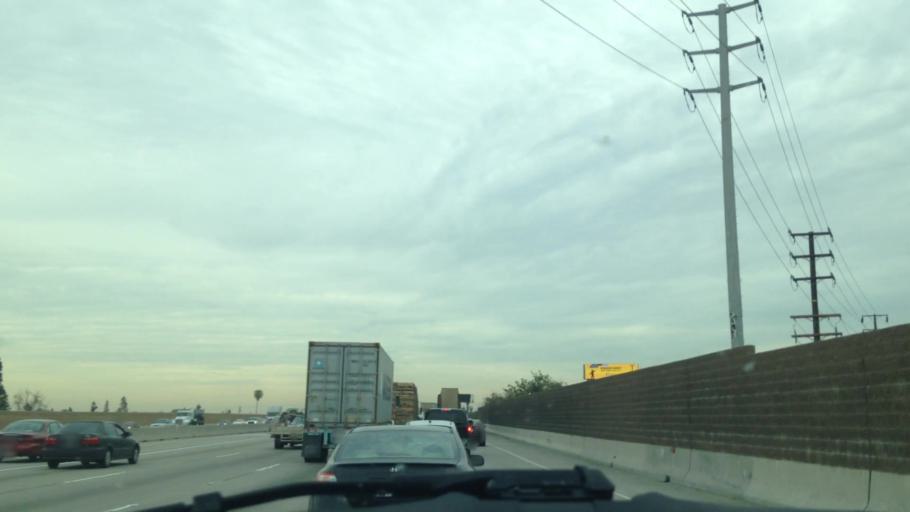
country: US
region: California
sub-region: Orange County
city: Placentia
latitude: 33.8705
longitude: -117.8802
